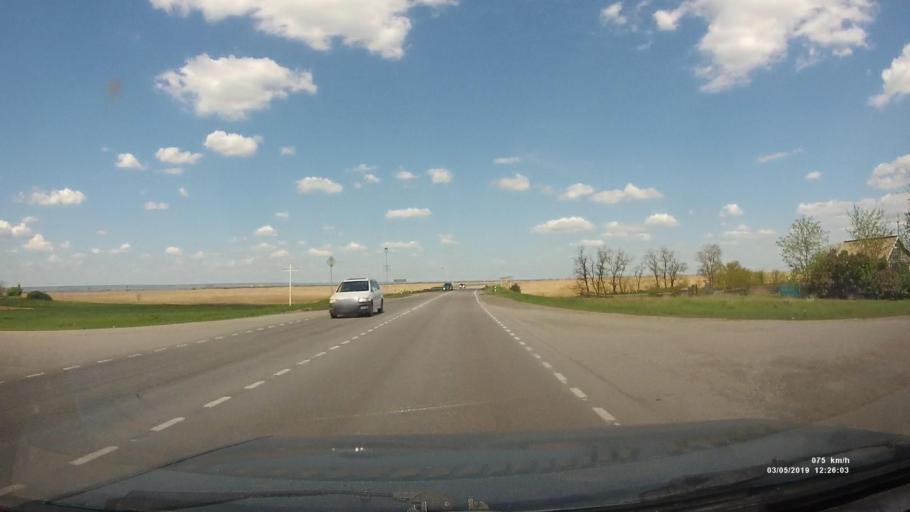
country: RU
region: Rostov
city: Semikarakorsk
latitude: 47.4401
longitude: 40.7120
